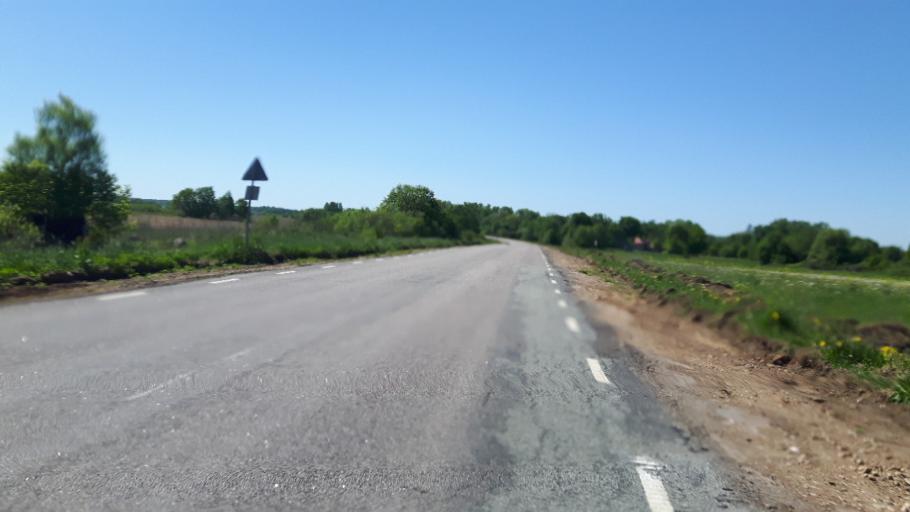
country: EE
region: Ida-Virumaa
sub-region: Narva-Joesuu linn
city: Narva-Joesuu
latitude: 59.3956
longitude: 27.9273
